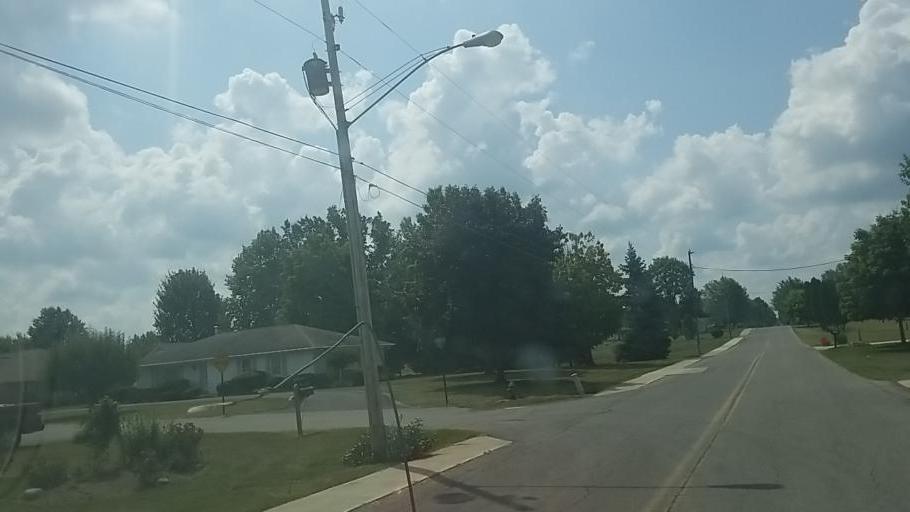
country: US
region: Ohio
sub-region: Wyandot County
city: Upper Sandusky
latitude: 40.8392
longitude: -83.2845
